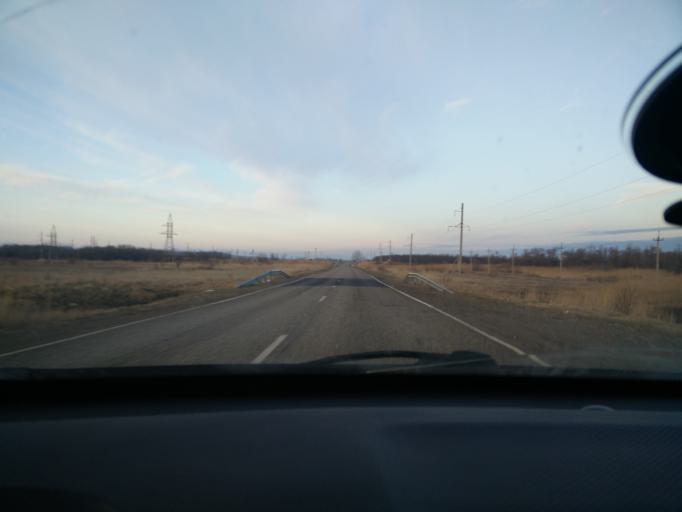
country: RU
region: Stavropol'skiy
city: Tatarka
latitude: 44.9972
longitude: 41.7561
